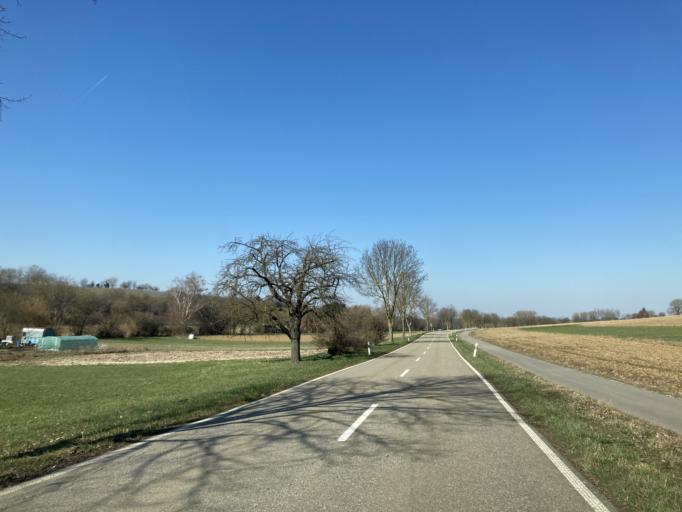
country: DE
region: Baden-Wuerttemberg
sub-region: Freiburg Region
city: Buggingen
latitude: 47.8250
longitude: 7.6531
